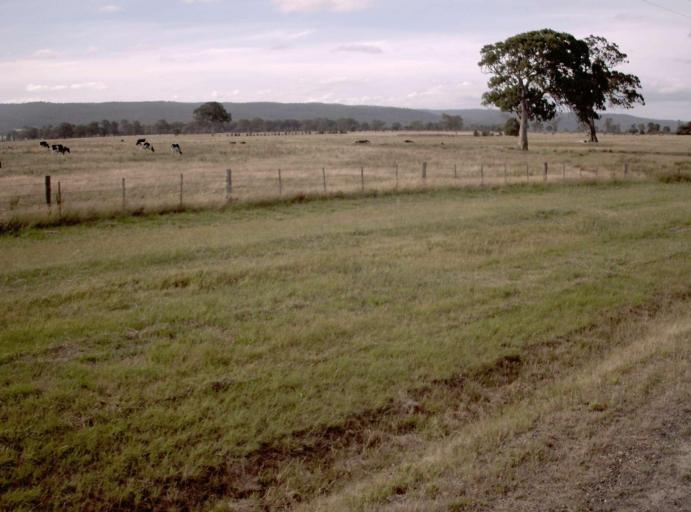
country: AU
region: Victoria
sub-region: Wellington
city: Heyfield
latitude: -38.0443
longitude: 146.6651
